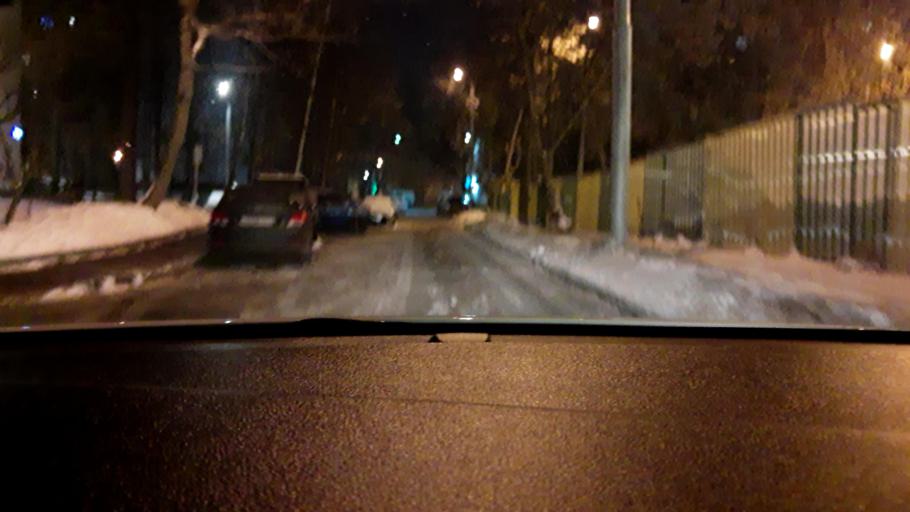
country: RU
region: Moscow
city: Leonovo
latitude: 55.8864
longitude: 37.6489
